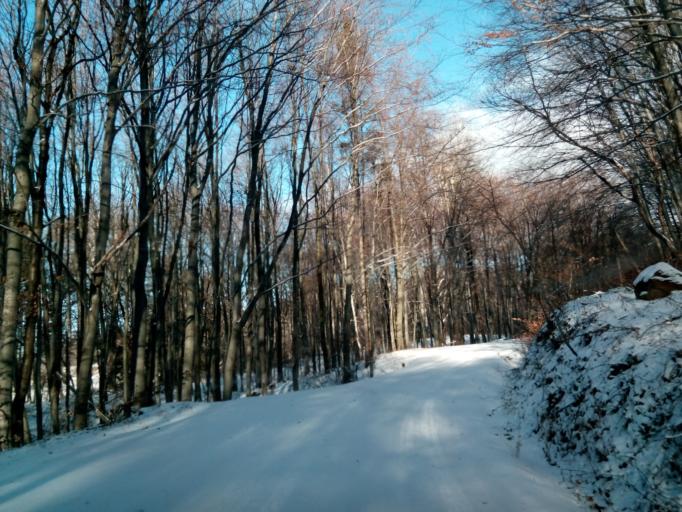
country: HU
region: Borsod-Abauj-Zemplen
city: Gonc
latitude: 48.5732
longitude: 21.4384
